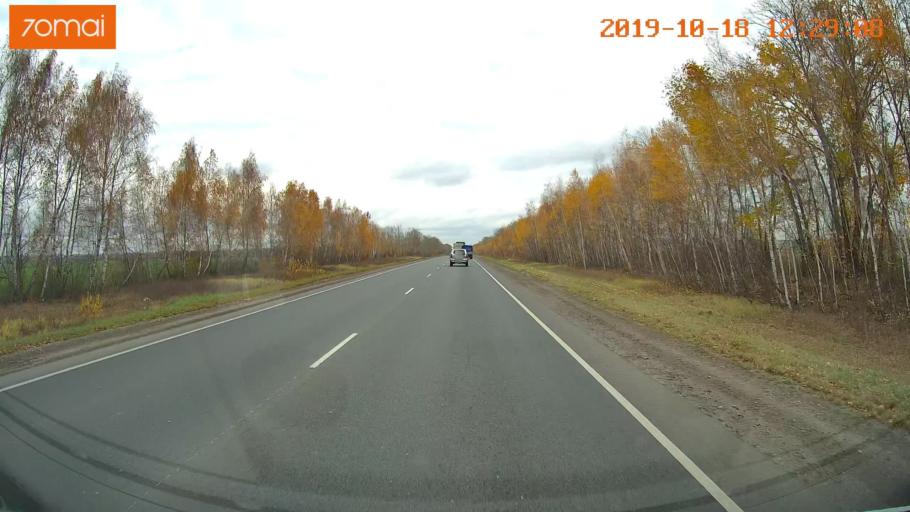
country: RU
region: Rjazan
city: Ryazan'
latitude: 54.5766
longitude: 39.5796
